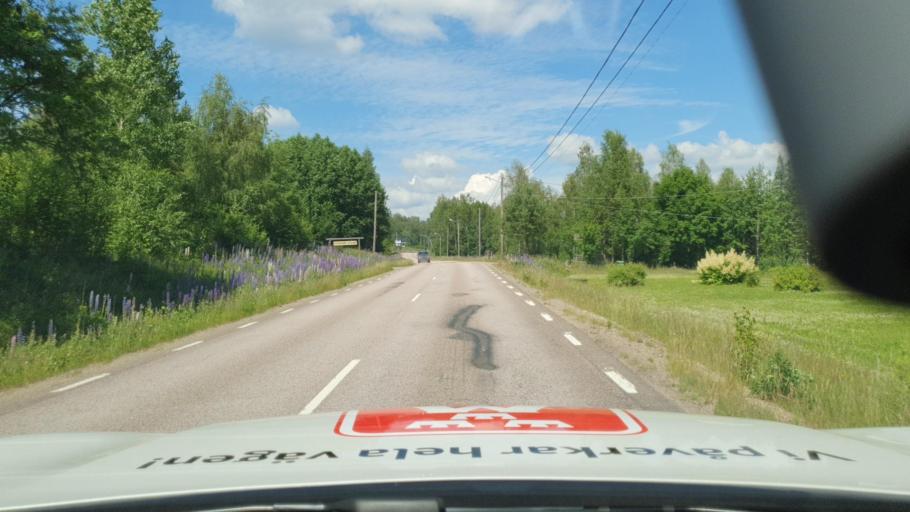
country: SE
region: Vaermland
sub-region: Torsby Kommun
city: Torsby
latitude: 60.3110
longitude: 13.0141
